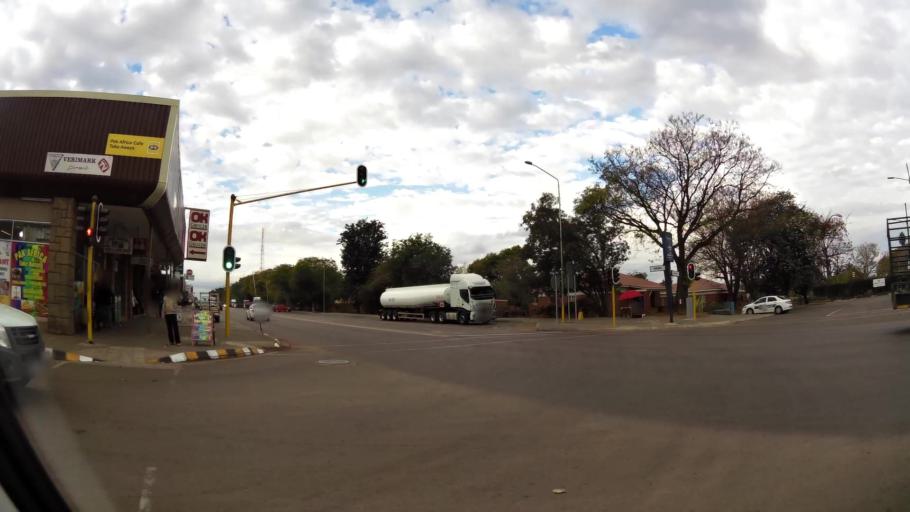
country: ZA
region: Limpopo
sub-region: Waterberg District Municipality
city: Modimolle
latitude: -24.5224
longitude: 28.7112
